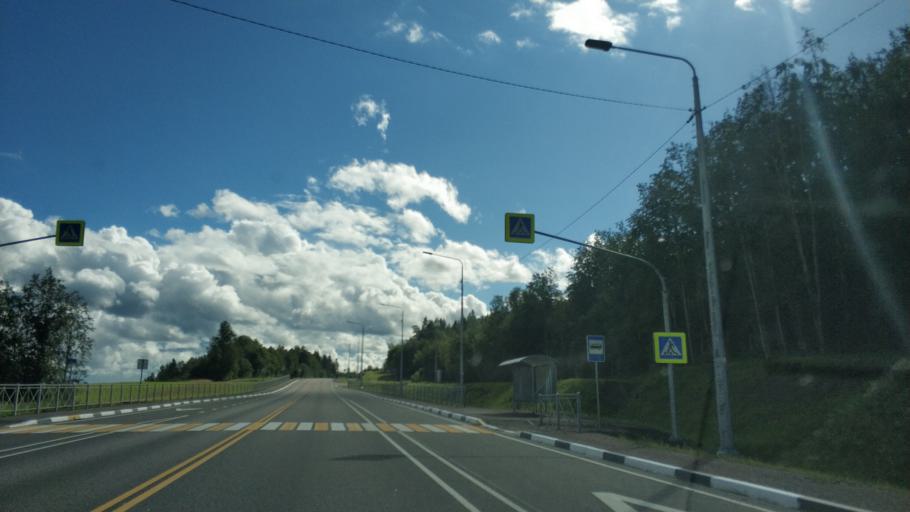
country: RU
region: Republic of Karelia
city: Ruskeala
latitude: 61.9032
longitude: 30.6341
